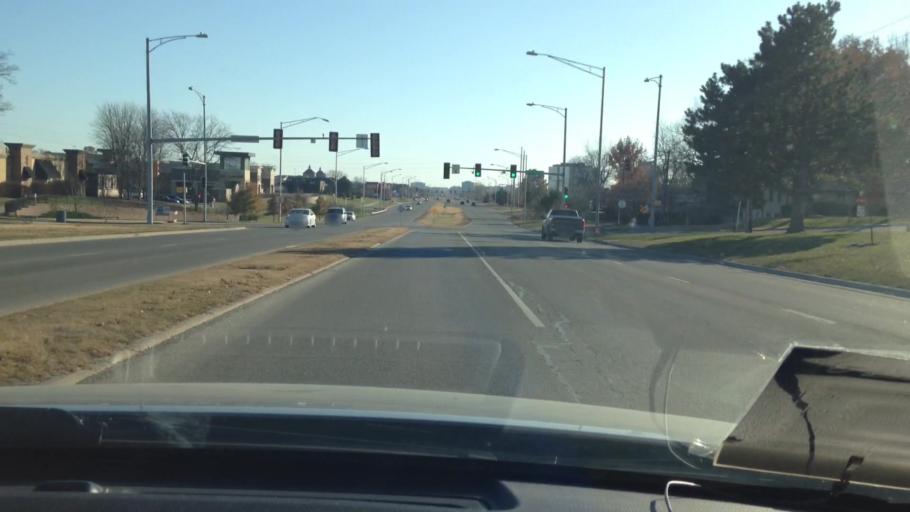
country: US
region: Kansas
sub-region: Johnson County
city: Overland Park
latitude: 38.9685
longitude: -94.6676
